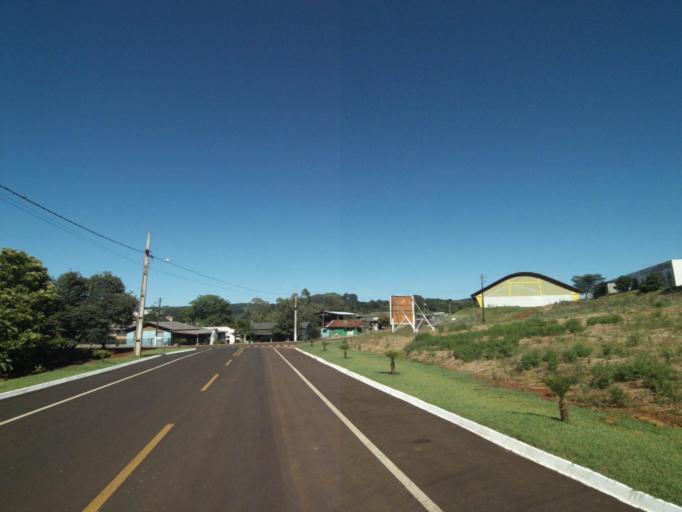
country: BR
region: Parana
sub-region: Pato Branco
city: Pato Branco
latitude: -26.2641
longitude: -52.7761
